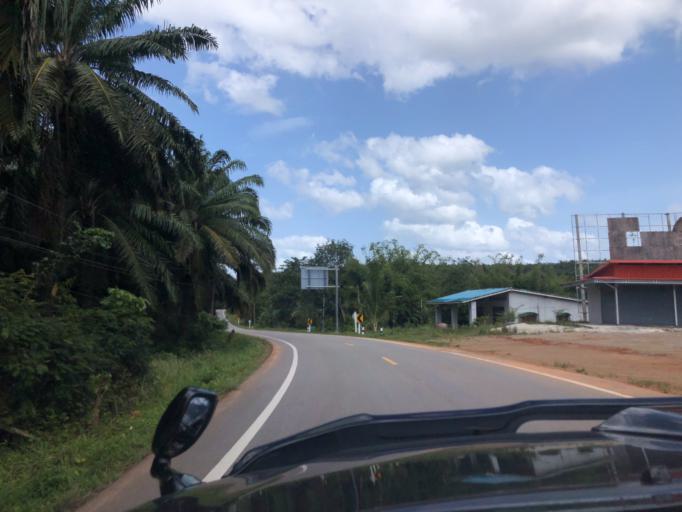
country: TH
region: Krabi
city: Khlong Thom
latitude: 7.9486
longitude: 99.2065
